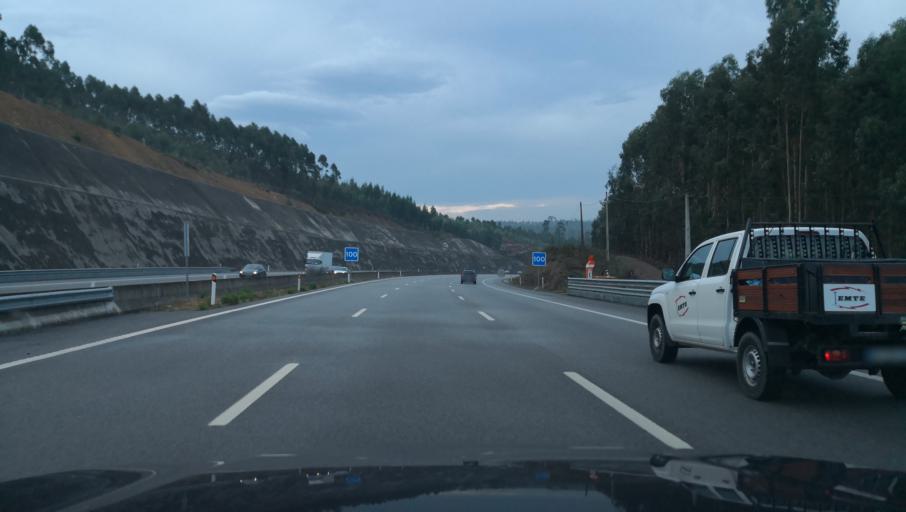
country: PT
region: Porto
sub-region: Paredes
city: Recarei
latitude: 41.1146
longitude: -8.4323
